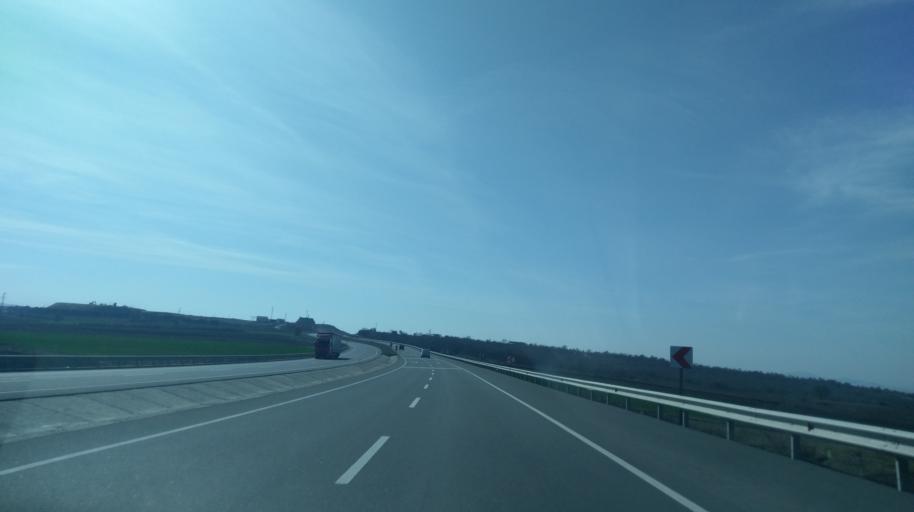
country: TR
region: Edirne
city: Kesan
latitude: 40.9322
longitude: 26.6359
